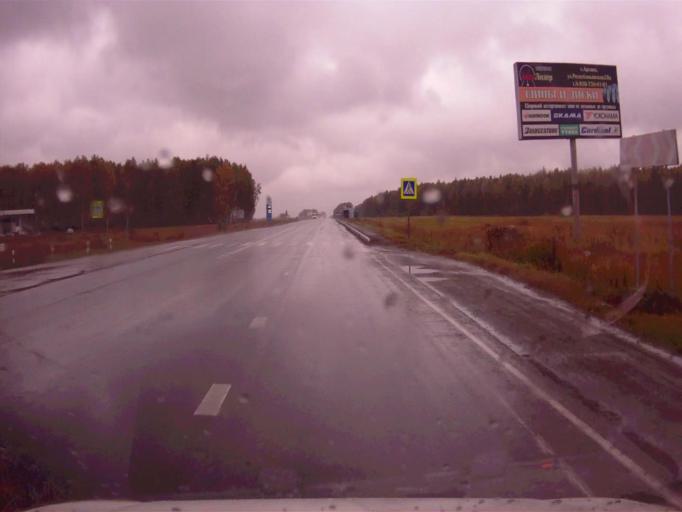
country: RU
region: Chelyabinsk
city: Argayash
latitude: 55.4174
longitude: 61.0251
